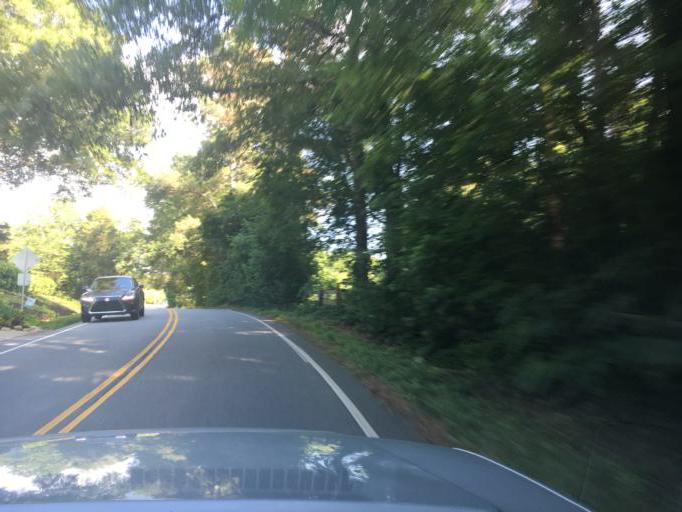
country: US
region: South Carolina
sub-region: Greenville County
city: Simpsonville
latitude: 34.7726
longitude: -82.2666
